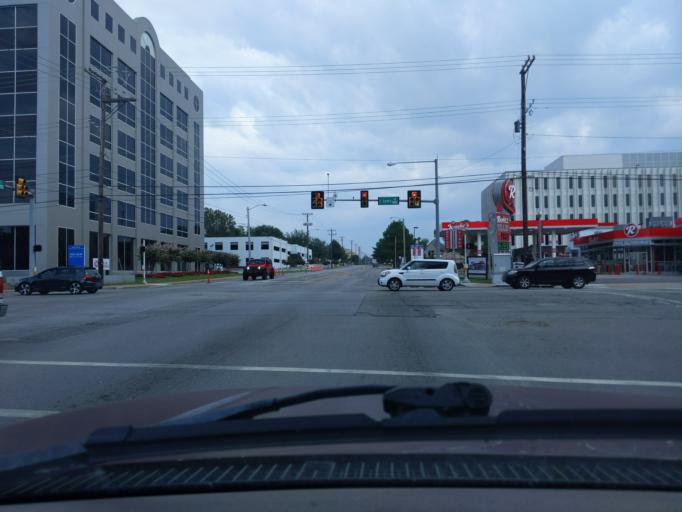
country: US
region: Oklahoma
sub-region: Tulsa County
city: Tulsa
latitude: 36.1332
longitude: -95.9585
